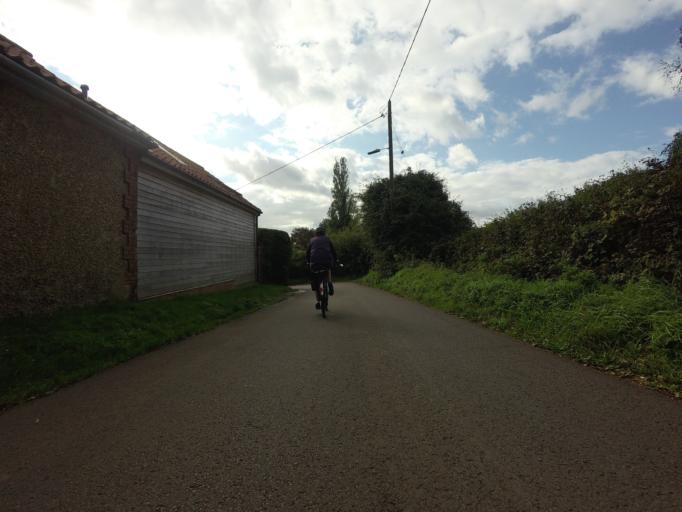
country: GB
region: England
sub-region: Norfolk
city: Dersingham
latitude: 52.8488
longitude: 0.5093
